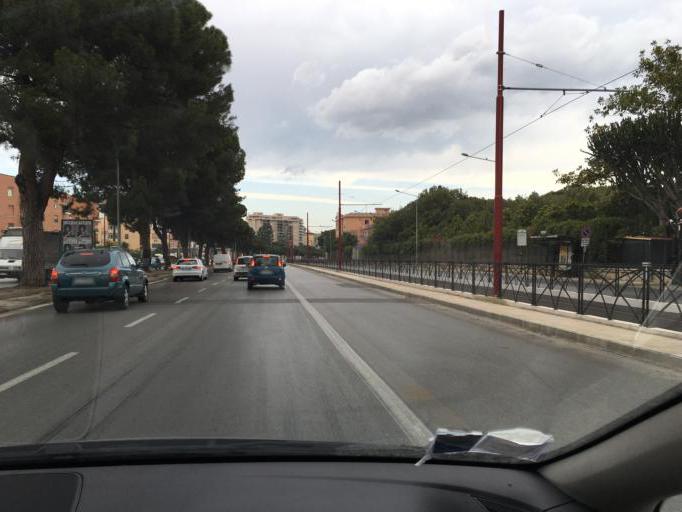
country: IT
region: Sicily
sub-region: Palermo
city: Palermo
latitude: 38.1171
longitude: 13.3293
